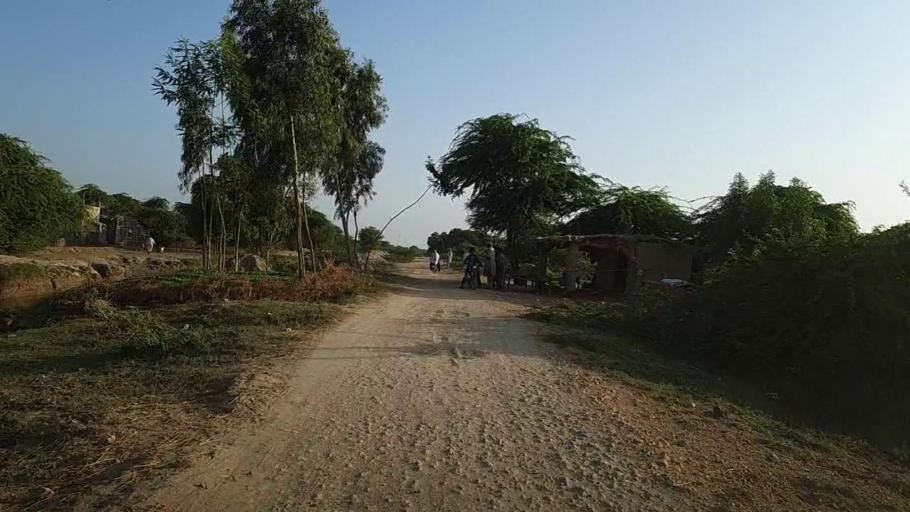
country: PK
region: Sindh
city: Kario
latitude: 24.7229
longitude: 68.6674
